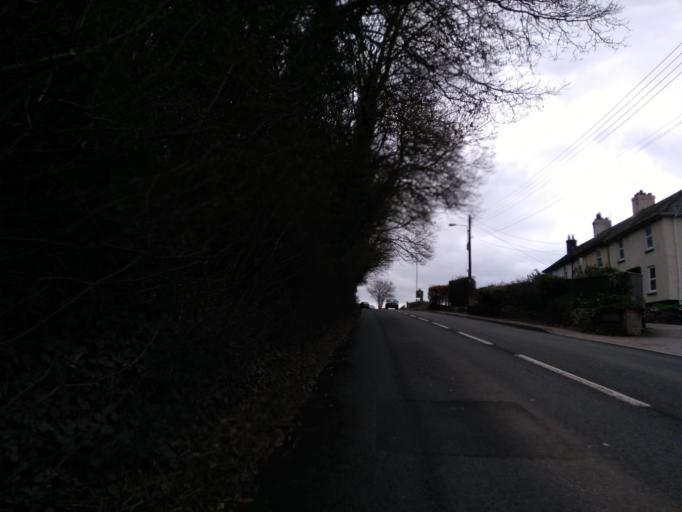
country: GB
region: England
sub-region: Devon
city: Exeter
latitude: 50.7556
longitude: -3.5547
